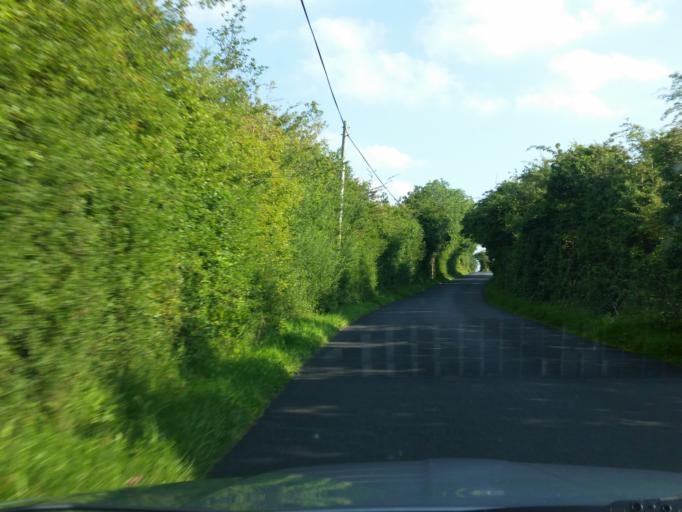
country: GB
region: Northern Ireland
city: Lisnaskea
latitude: 54.2362
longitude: -7.3667
